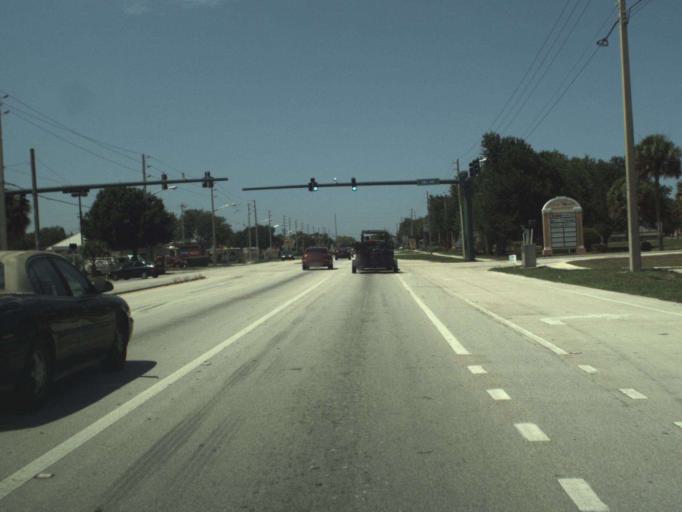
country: US
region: Florida
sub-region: Saint Lucie County
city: Fort Pierce South
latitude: 27.4118
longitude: -80.3259
